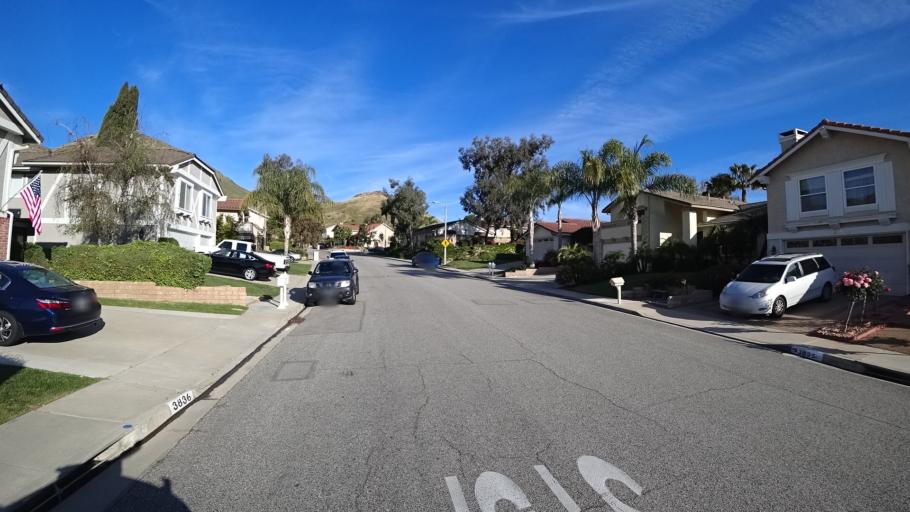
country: US
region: California
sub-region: Ventura County
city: Casa Conejo
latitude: 34.1875
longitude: -118.9576
